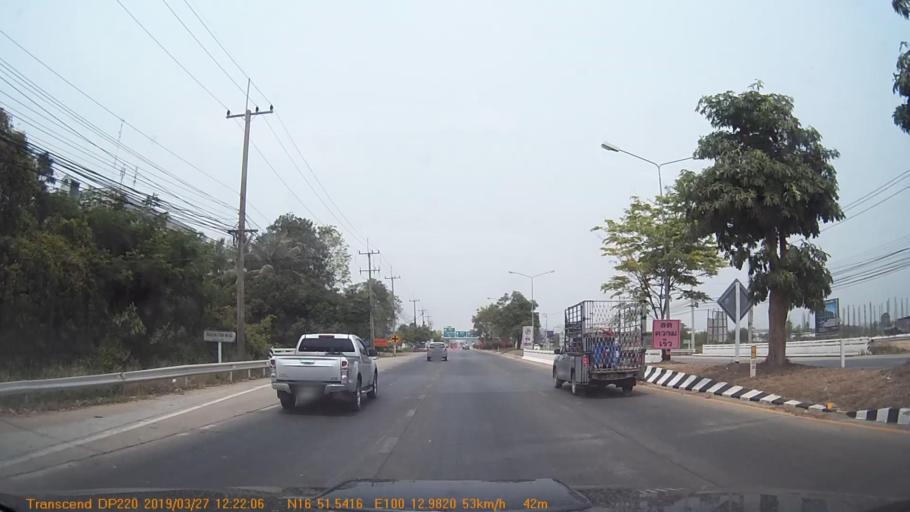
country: TH
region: Phitsanulok
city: Phitsanulok
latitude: 16.8592
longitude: 100.2163
